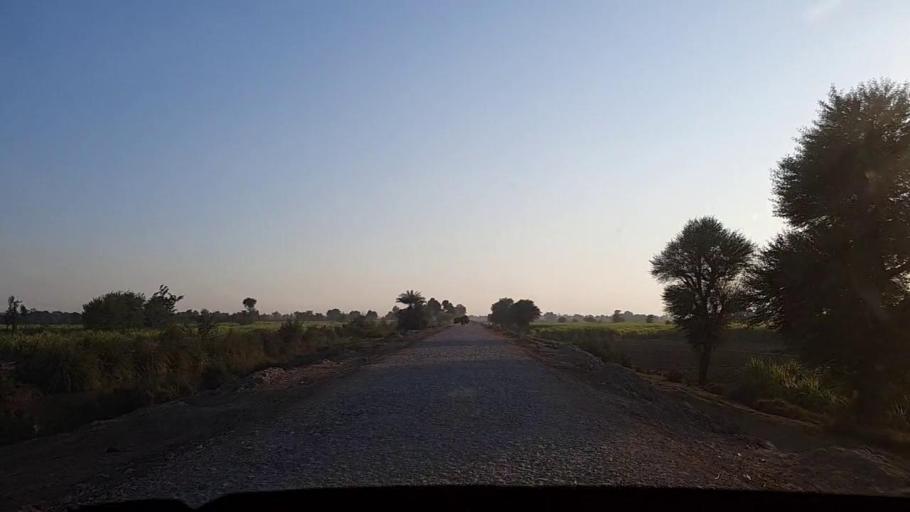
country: PK
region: Sindh
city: Sobhadero
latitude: 27.3737
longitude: 68.3787
